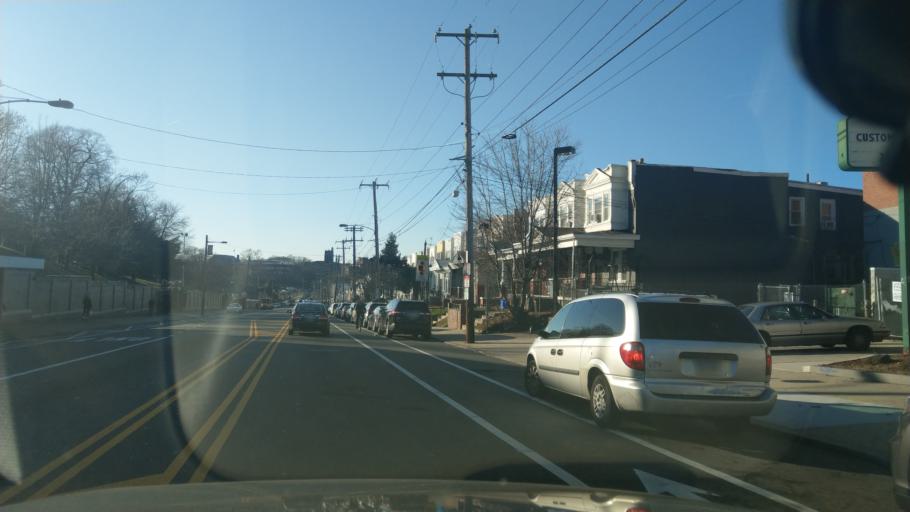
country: US
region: Pennsylvania
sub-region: Montgomery County
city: Wyncote
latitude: 40.0391
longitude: -75.1449
